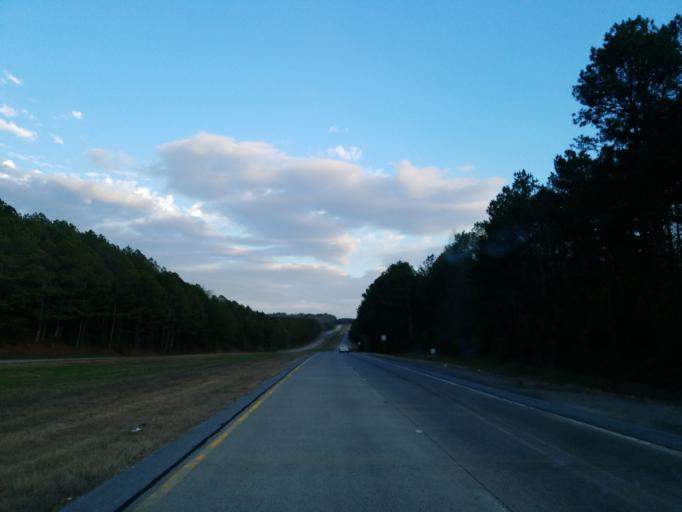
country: US
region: Georgia
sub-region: Pickens County
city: Nelson
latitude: 34.3807
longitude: -84.3907
